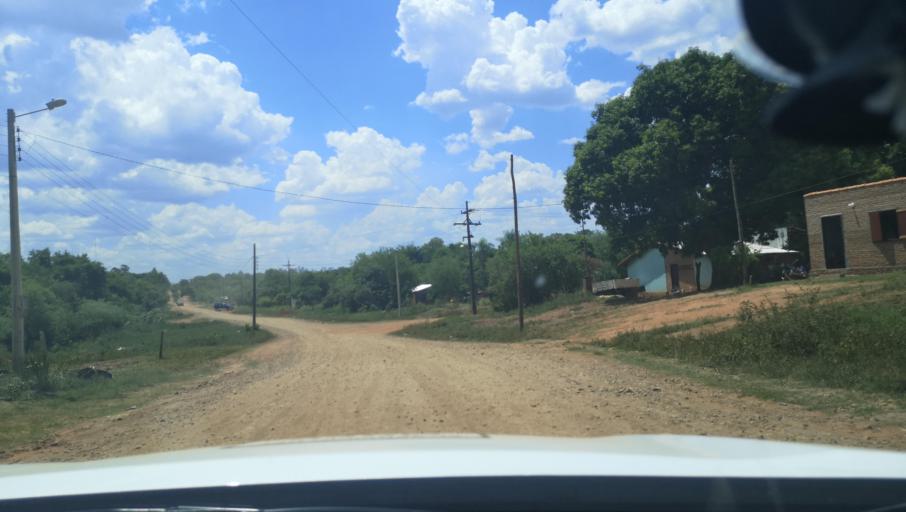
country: PY
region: Itapua
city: Carmen del Parana
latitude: -27.1721
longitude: -56.2485
